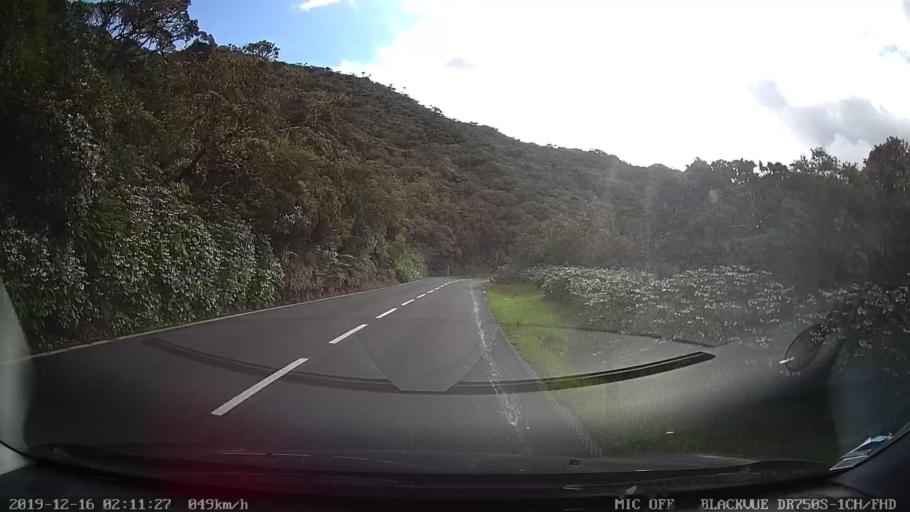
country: RE
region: Reunion
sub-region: Reunion
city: Cilaos
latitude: -21.1622
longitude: 55.5959
